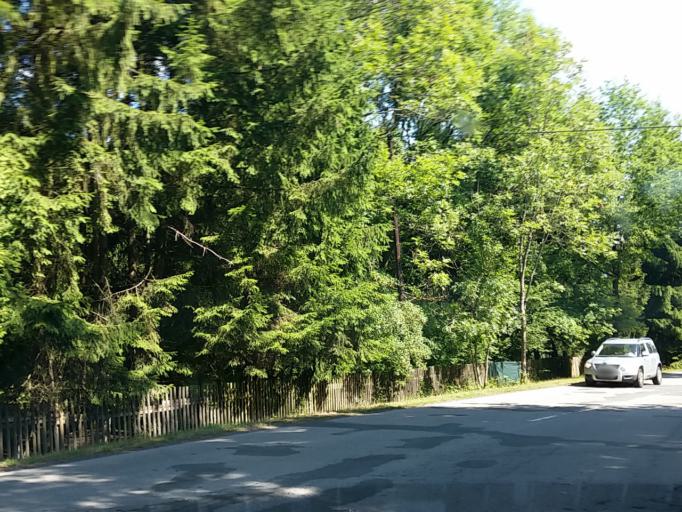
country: DE
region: Saarland
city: Lebach
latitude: 49.4288
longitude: 6.8929
